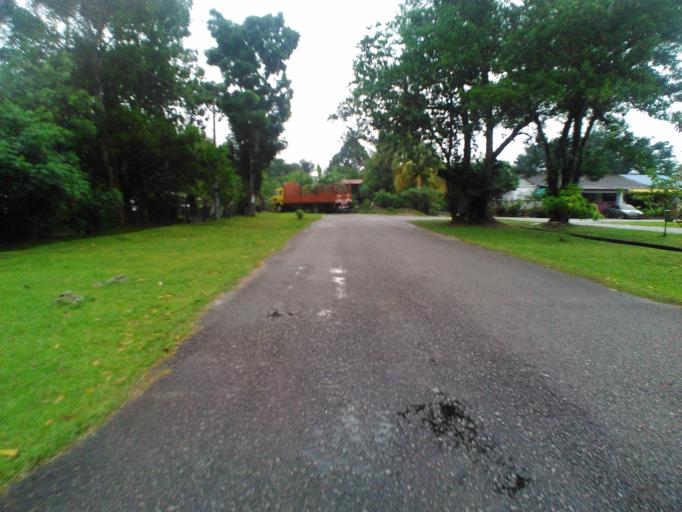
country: MY
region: Kedah
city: Kulim
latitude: 5.3618
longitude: 100.5745
